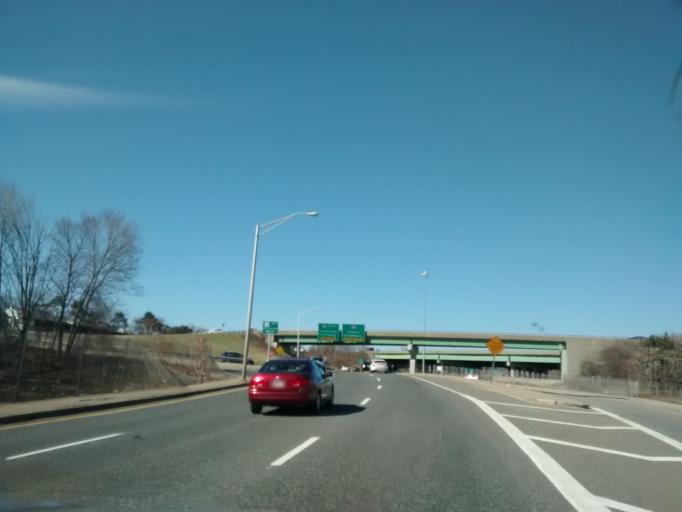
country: US
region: Massachusetts
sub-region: Worcester County
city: Worcester
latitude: 42.2942
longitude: -71.8027
